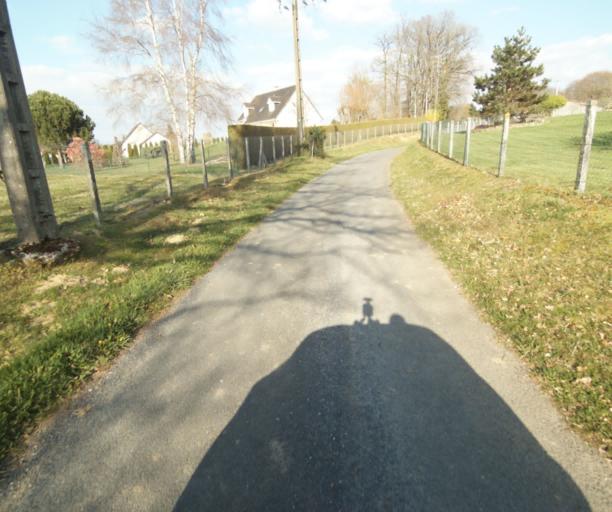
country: FR
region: Limousin
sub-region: Departement de la Correze
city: Saint-Clement
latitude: 45.3491
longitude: 1.6327
